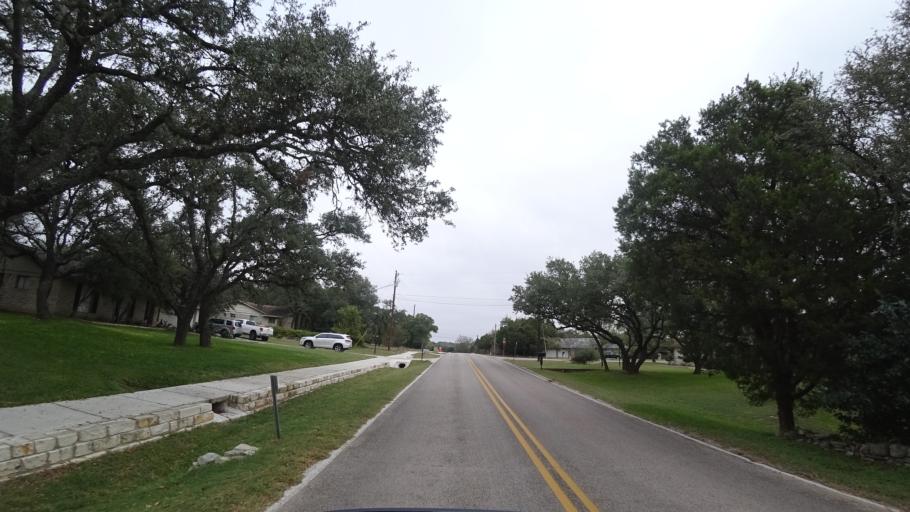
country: US
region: Texas
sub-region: Travis County
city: Barton Creek
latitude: 30.2286
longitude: -97.8966
